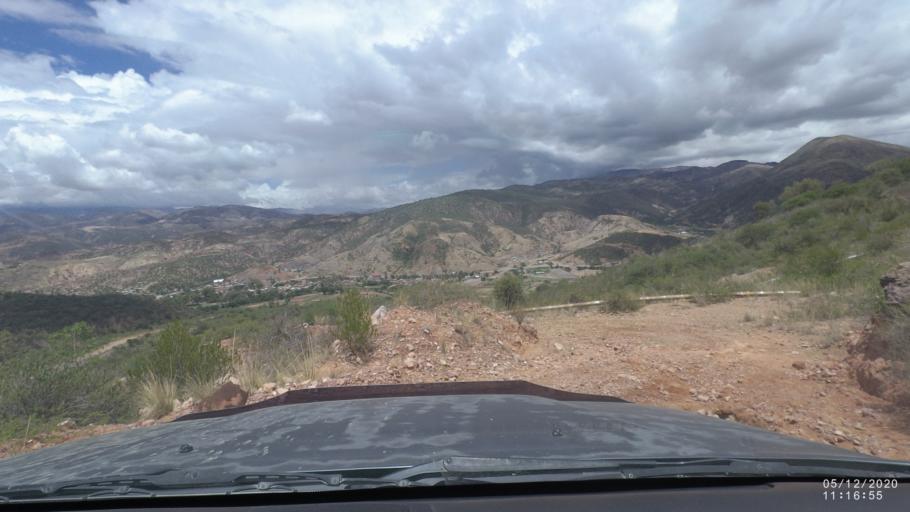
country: BO
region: Cochabamba
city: Sipe Sipe
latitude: -17.5514
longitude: -66.3305
